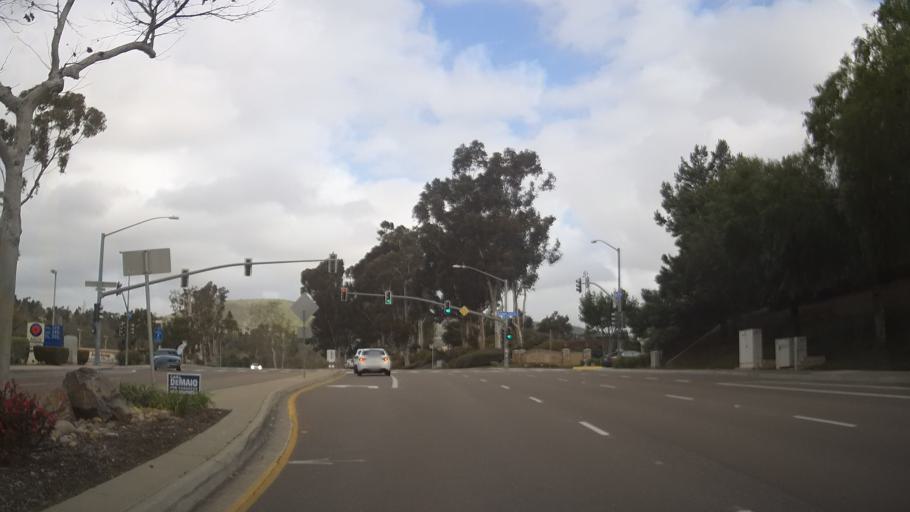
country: US
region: California
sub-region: San Diego County
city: Poway
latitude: 32.9486
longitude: -117.0955
